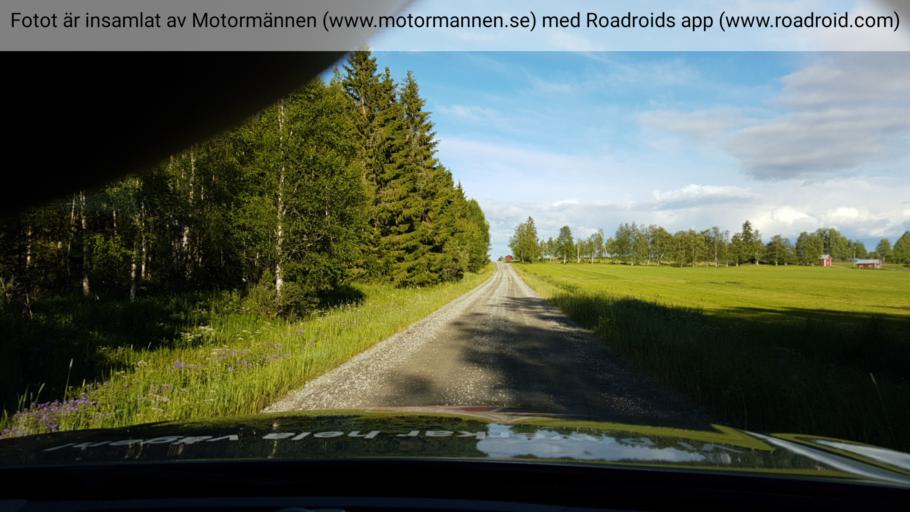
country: SE
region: Jaemtland
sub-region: Bergs Kommun
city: Hoverberg
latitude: 62.9358
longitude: 14.4160
